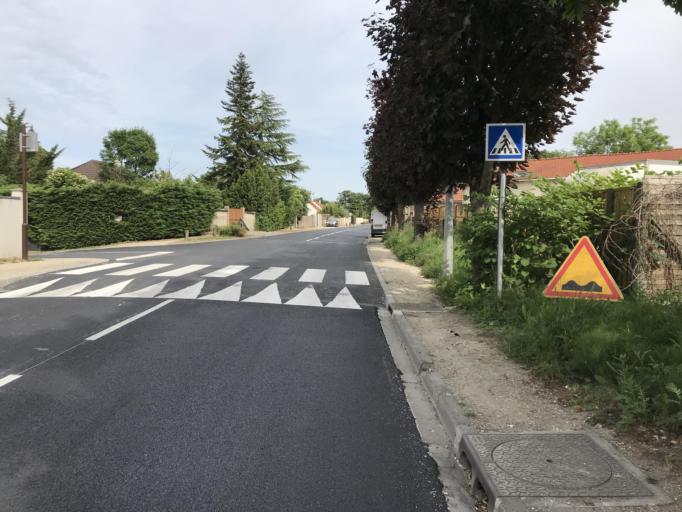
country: FR
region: Ile-de-France
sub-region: Departement de l'Essonne
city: La Ville-du-Bois
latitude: 48.6480
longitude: 2.2573
